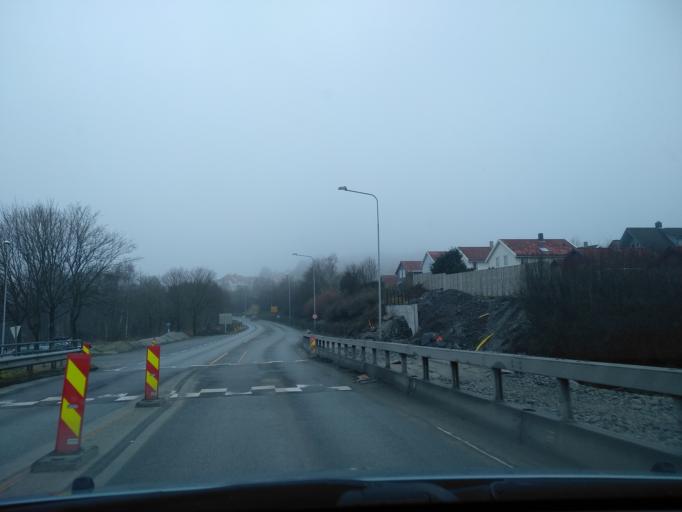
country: NO
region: Rogaland
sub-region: Stavanger
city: Stavanger
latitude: 58.9804
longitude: 5.6834
